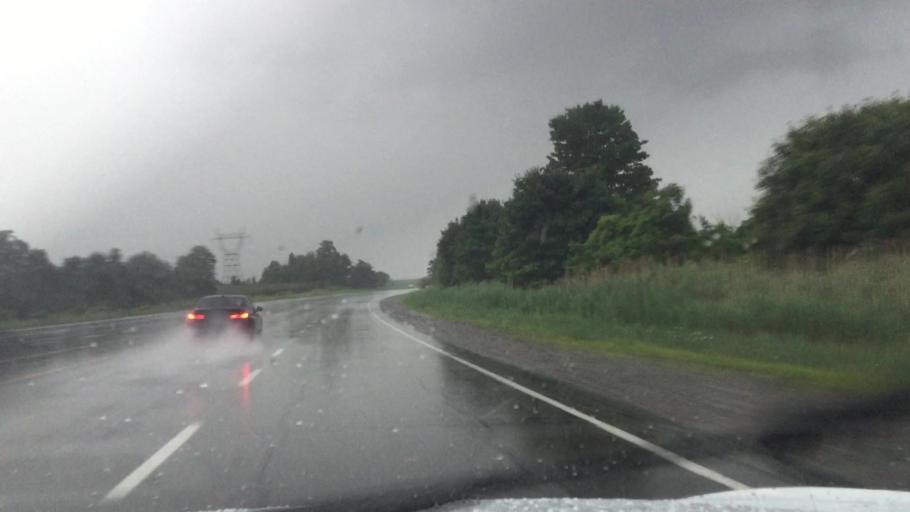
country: CA
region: Ontario
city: Pickering
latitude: 43.8633
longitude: -79.1472
